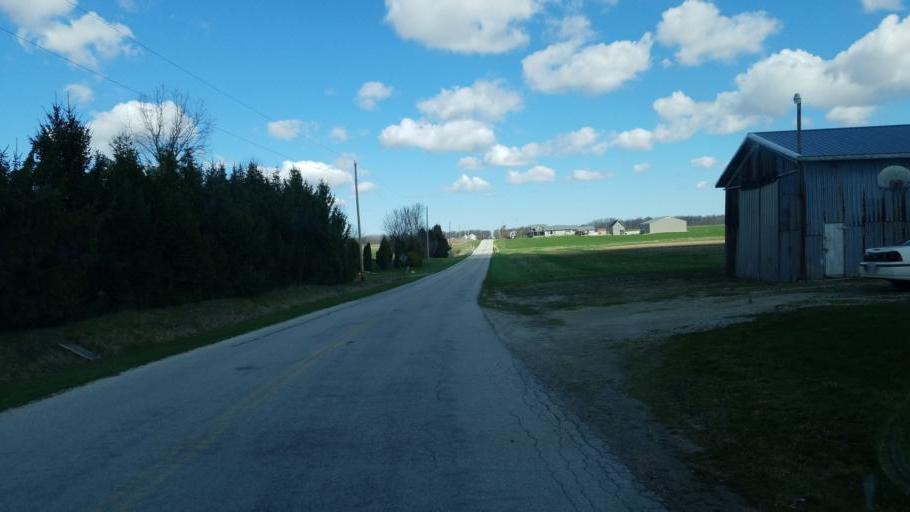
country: US
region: Ohio
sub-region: Sandusky County
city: Mount Carmel
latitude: 41.1687
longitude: -82.9382
